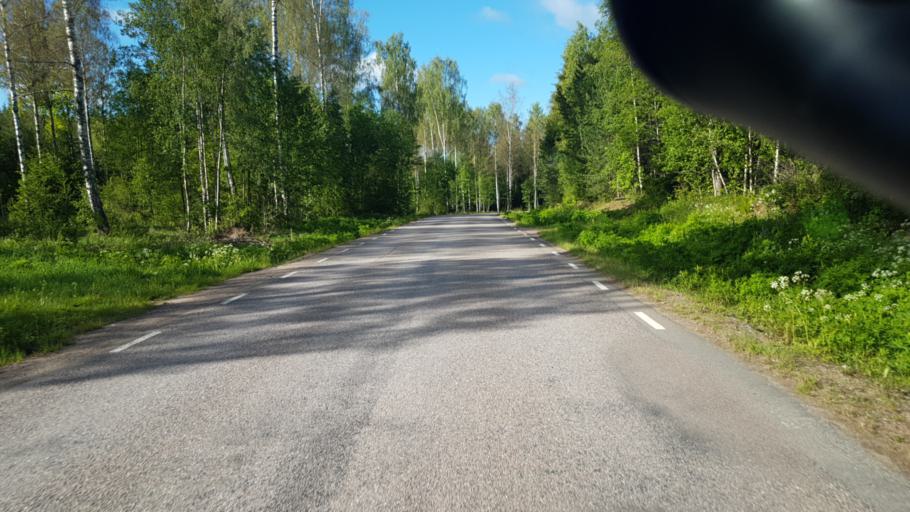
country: SE
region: Vaermland
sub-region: Arvika Kommun
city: Arvika
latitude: 59.5790
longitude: 12.7224
